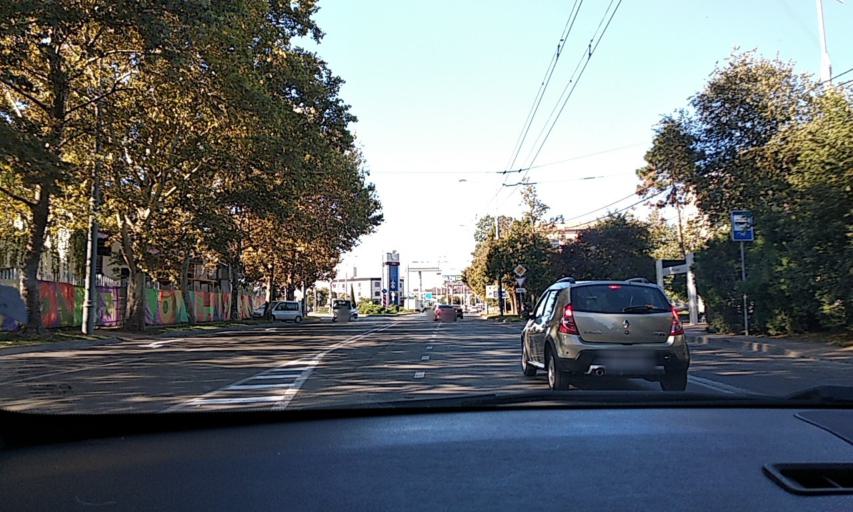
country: RU
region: Krasnodarskiy
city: Pashkovskiy
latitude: 45.0165
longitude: 39.0953
